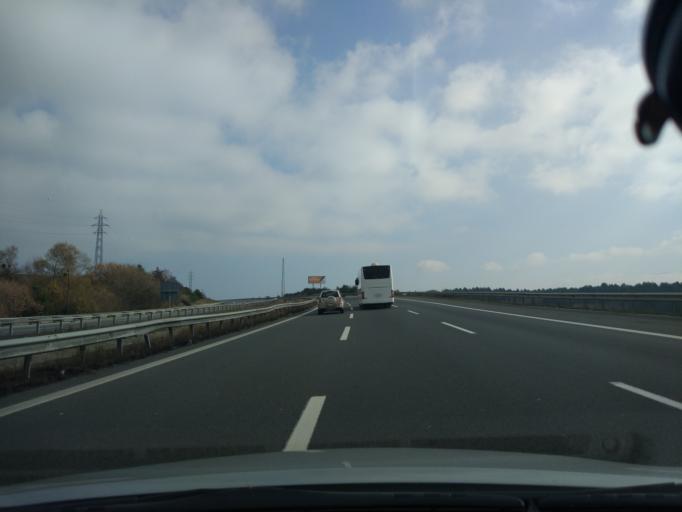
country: TR
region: Bolu
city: Bolu
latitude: 40.7682
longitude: 31.6499
